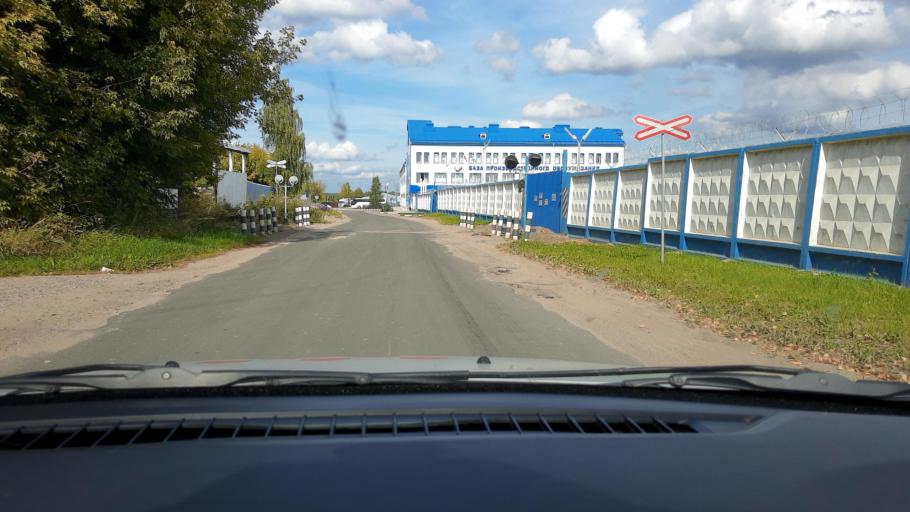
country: RU
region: Nizjnij Novgorod
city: Kstovo
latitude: 56.1290
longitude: 44.1374
